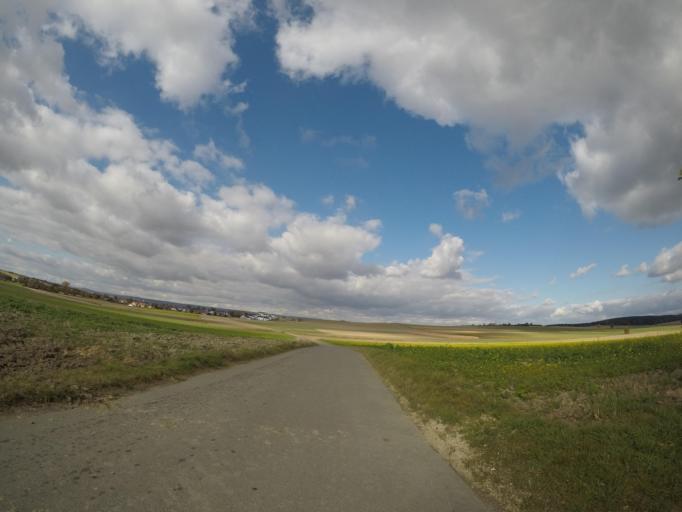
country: DE
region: Baden-Wuerttemberg
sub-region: Tuebingen Region
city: Unterstadion
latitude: 48.1963
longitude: 9.7011
